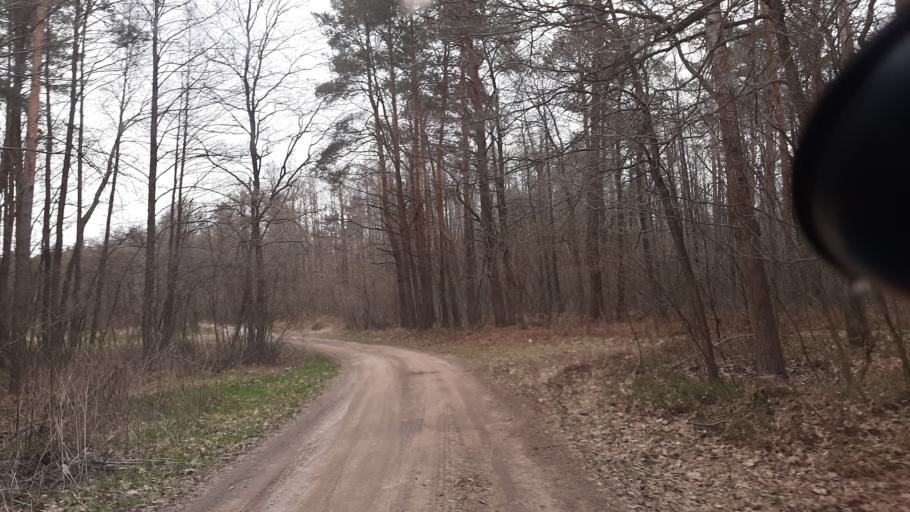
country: PL
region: Lublin Voivodeship
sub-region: Powiat lubartowski
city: Abramow
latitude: 51.4405
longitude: 22.3454
